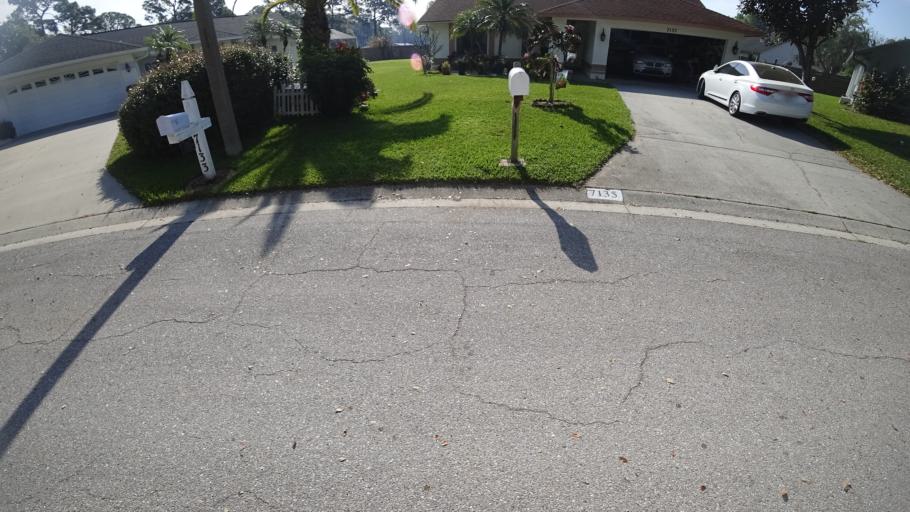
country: US
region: Florida
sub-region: Manatee County
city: Whitfield
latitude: 27.4133
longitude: -82.5533
